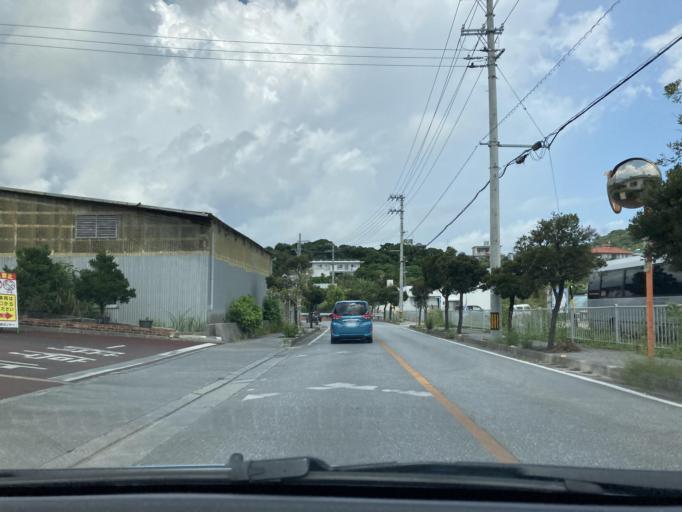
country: JP
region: Okinawa
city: Tomigusuku
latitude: 26.1693
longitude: 127.7544
